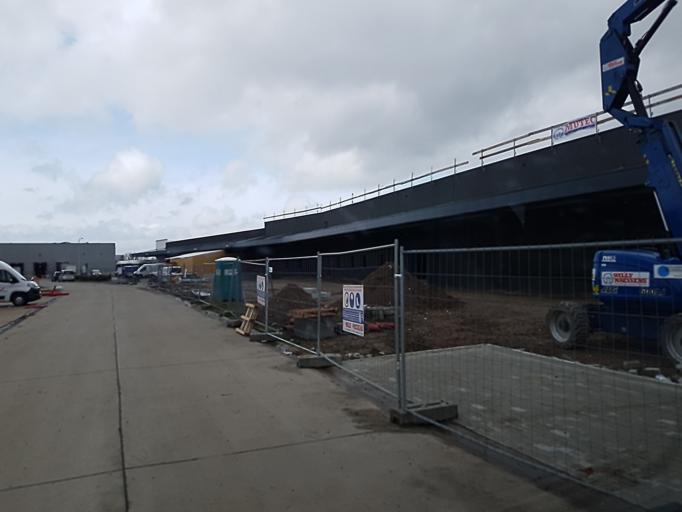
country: BE
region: Flanders
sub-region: Provincie Oost-Vlaanderen
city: Oudenaarde
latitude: 50.8399
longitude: 3.5942
